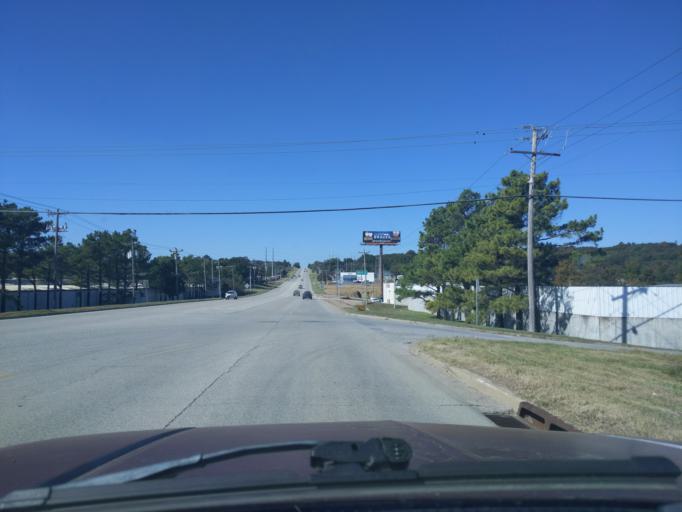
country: US
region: Oklahoma
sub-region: Tulsa County
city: Glenpool
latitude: 35.9885
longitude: -96.0293
